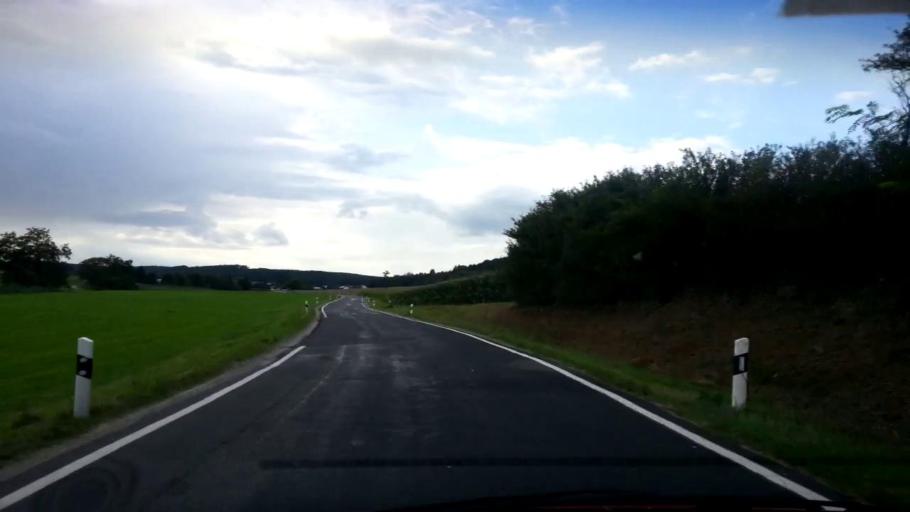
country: DE
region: Bavaria
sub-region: Regierungsbezirk Mittelfranken
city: Burghaslach
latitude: 49.7370
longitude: 10.5774
